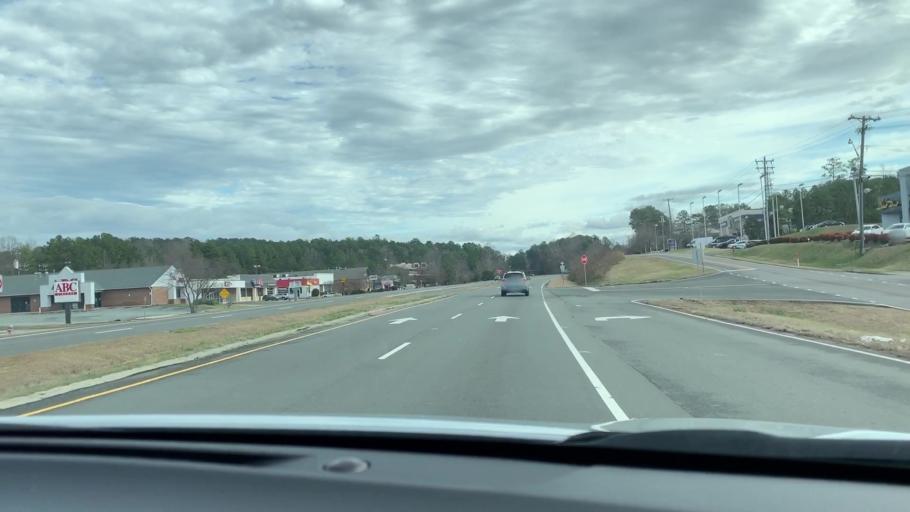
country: US
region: North Carolina
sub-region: Durham County
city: Durham
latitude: 35.9712
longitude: -78.9507
